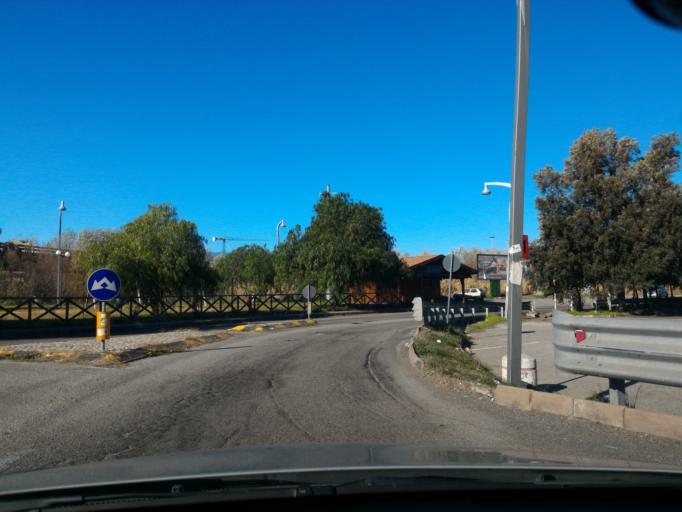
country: IT
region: Calabria
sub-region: Provincia di Cosenza
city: Cosenza
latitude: 39.3115
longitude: 16.2627
